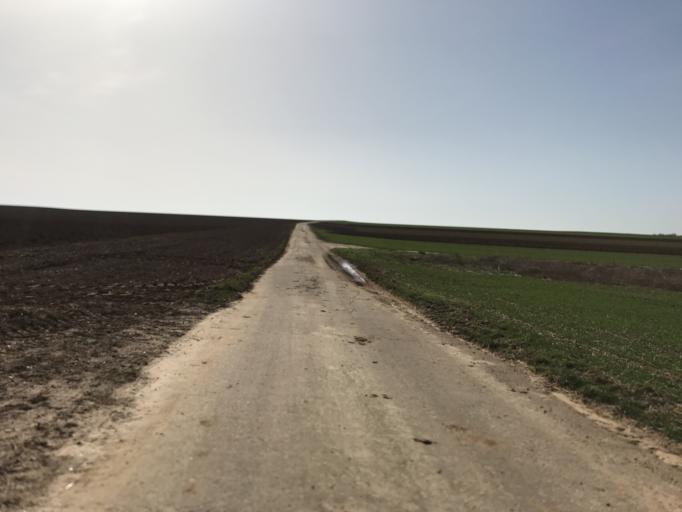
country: DE
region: Rheinland-Pfalz
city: Essenheim
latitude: 49.9376
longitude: 8.1405
